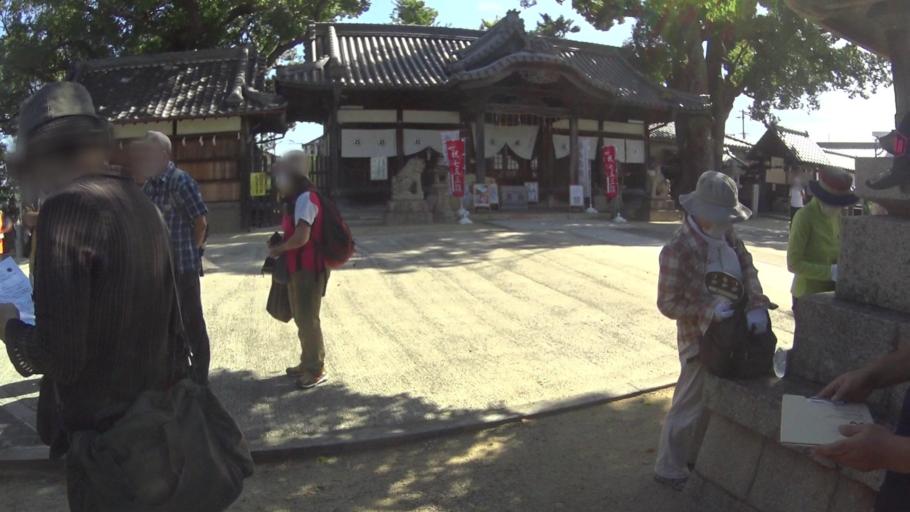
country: JP
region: Osaka
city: Takaishi
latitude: 34.5366
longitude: 135.4743
